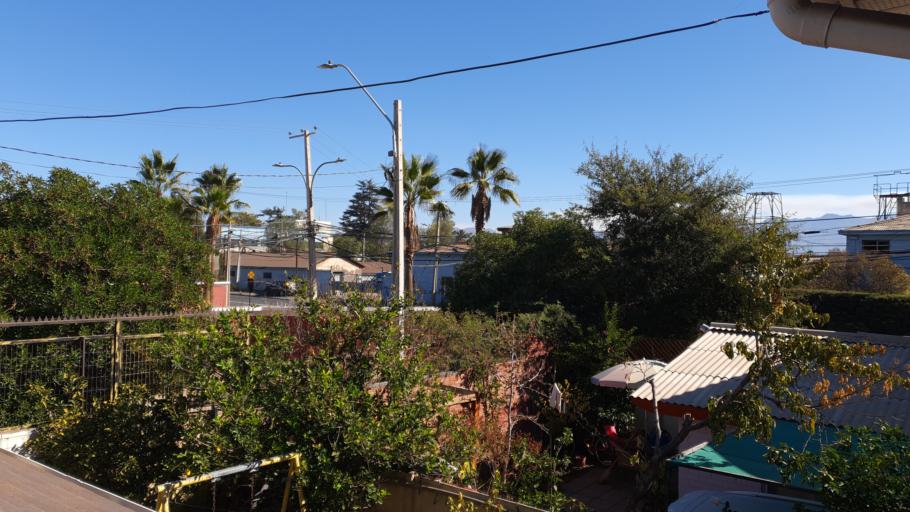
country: CL
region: Valparaiso
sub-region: Provincia de Los Andes
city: Los Andes
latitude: -32.8278
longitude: -70.5946
